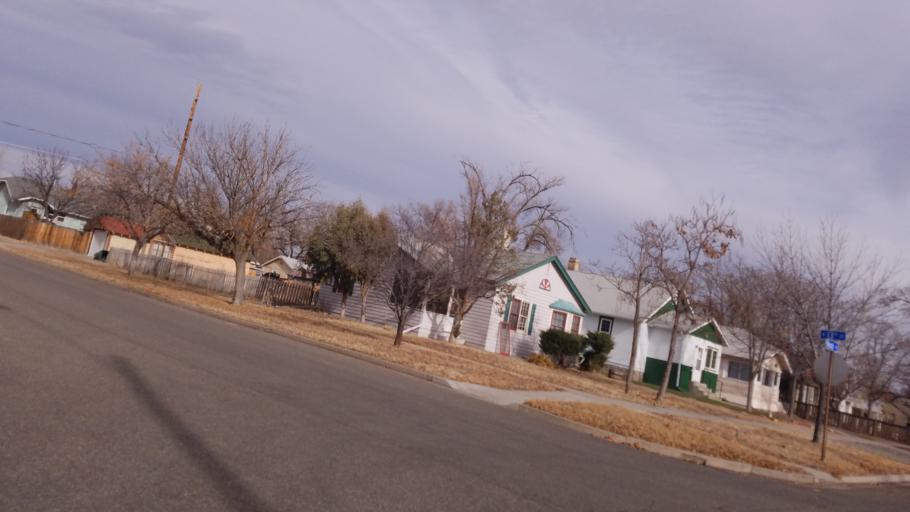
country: US
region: Colorado
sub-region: Mesa County
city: Grand Junction
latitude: 39.0687
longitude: -108.5509
